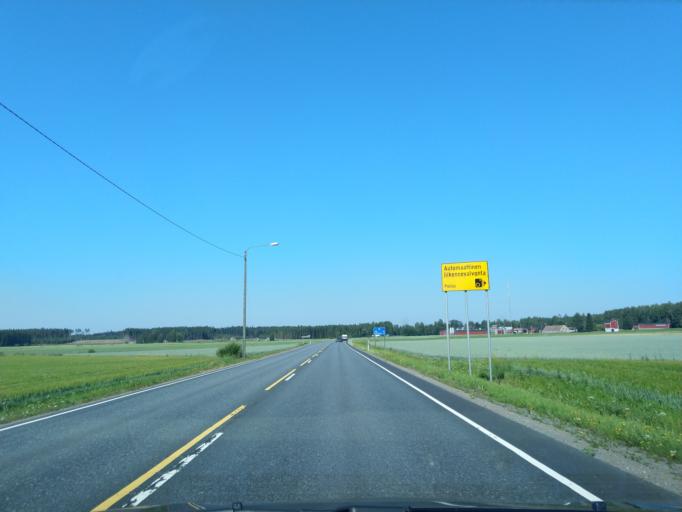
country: FI
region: Haeme
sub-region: Forssa
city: Humppila
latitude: 60.9738
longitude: 23.2493
